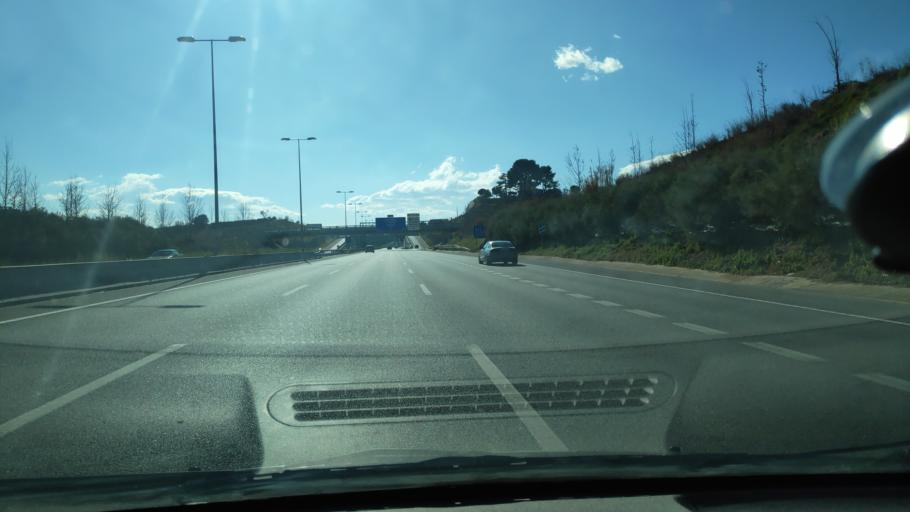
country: ES
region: Catalonia
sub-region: Provincia de Barcelona
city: Sant Quirze del Valles
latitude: 41.5554
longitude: 2.0778
